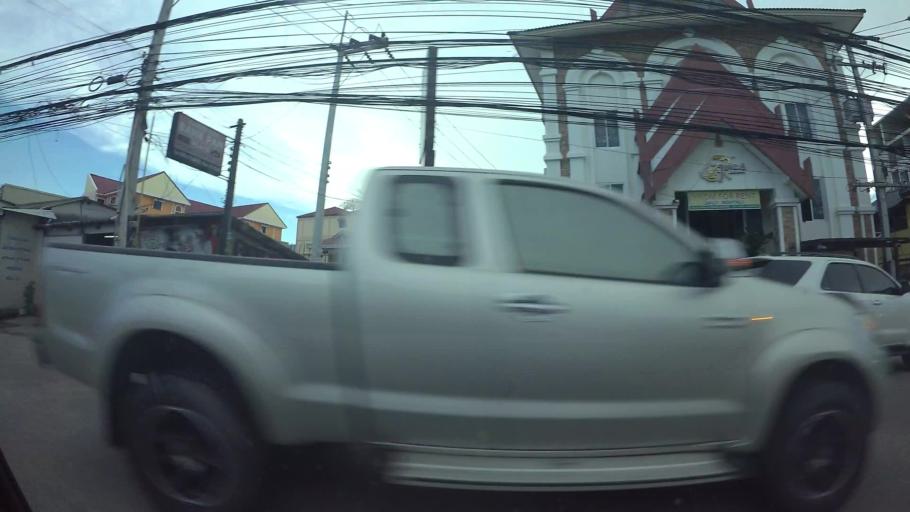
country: TH
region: Chon Buri
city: Phatthaya
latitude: 12.9106
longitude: 100.8855
